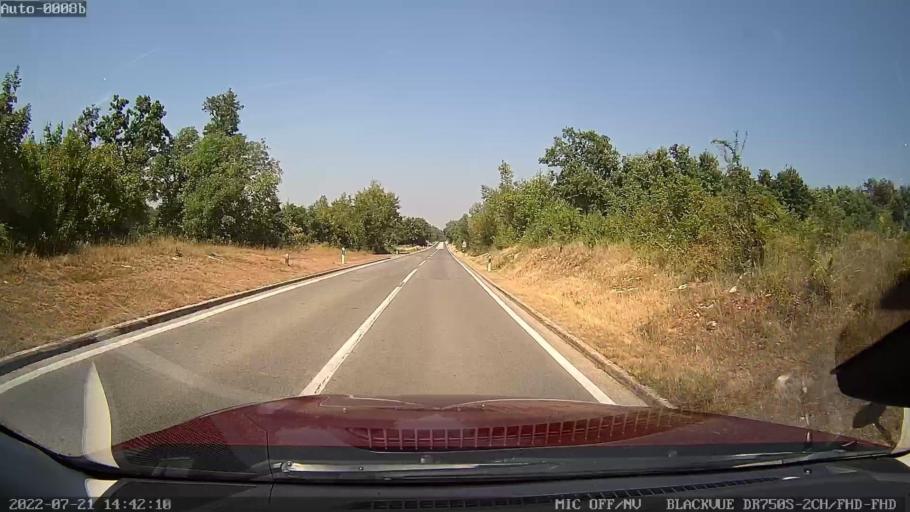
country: HR
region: Istarska
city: Vodnjan
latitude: 45.0954
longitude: 13.8810
